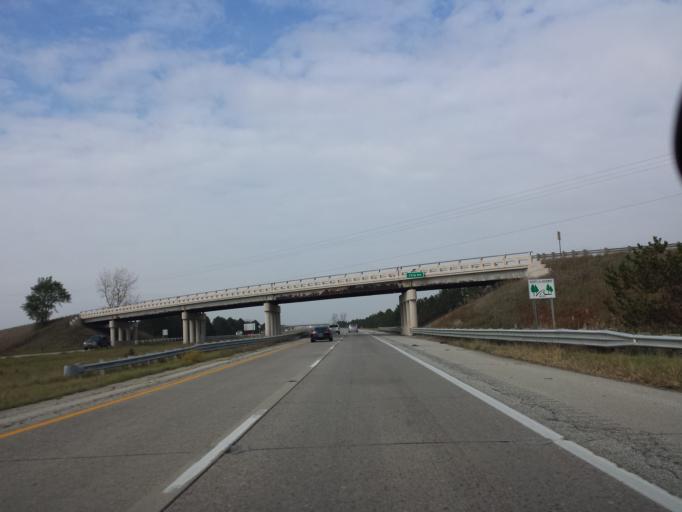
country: US
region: Michigan
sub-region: Bay County
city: Auburn
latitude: 43.6456
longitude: -83.9815
